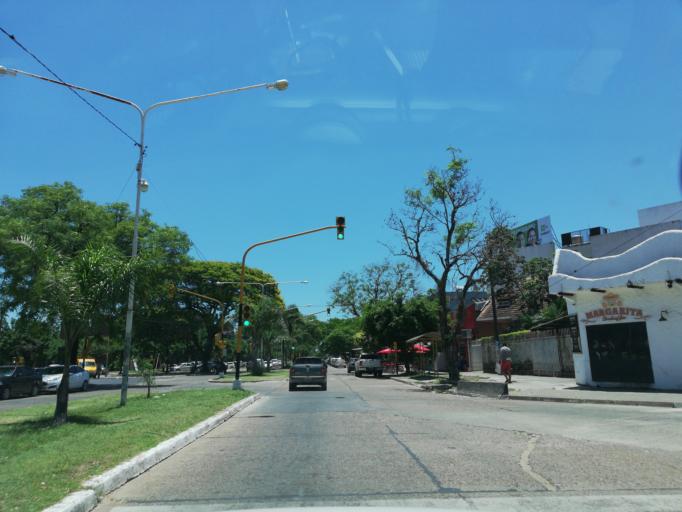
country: AR
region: Corrientes
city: Corrientes
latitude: -27.4630
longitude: -58.8267
